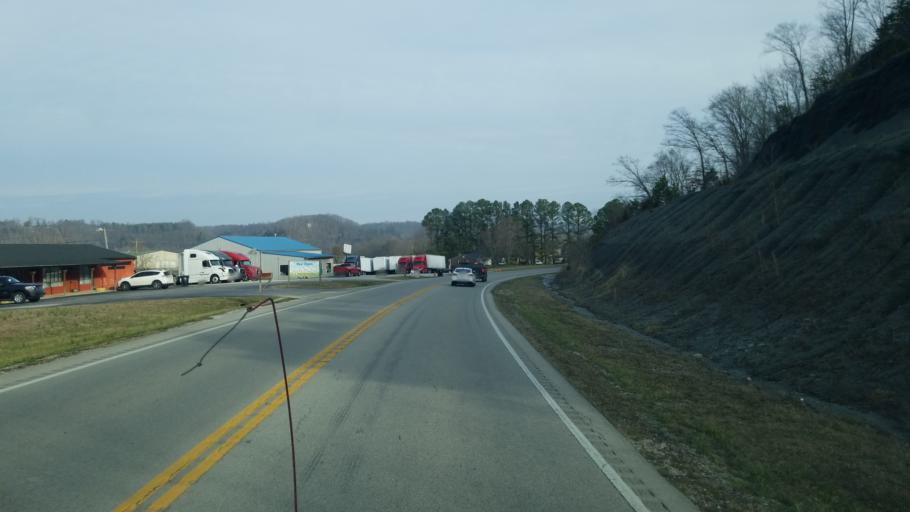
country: US
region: Kentucky
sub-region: Casey County
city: Liberty
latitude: 37.3062
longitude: -84.9454
